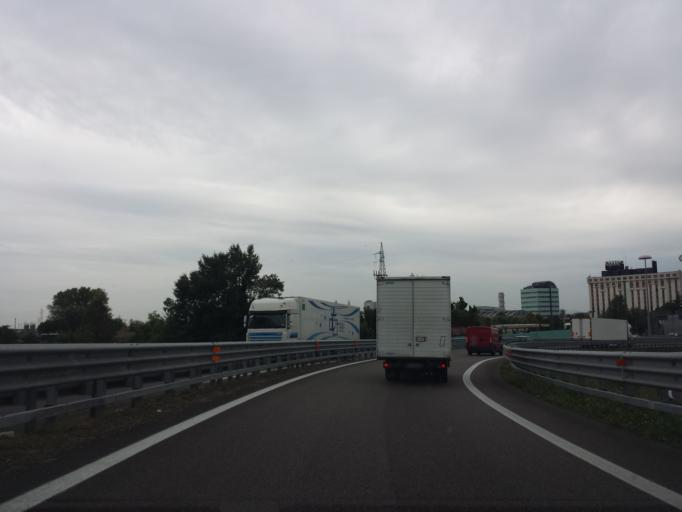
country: IT
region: Veneto
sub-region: Provincia di Padova
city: Noventa
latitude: 45.4185
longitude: 11.9380
